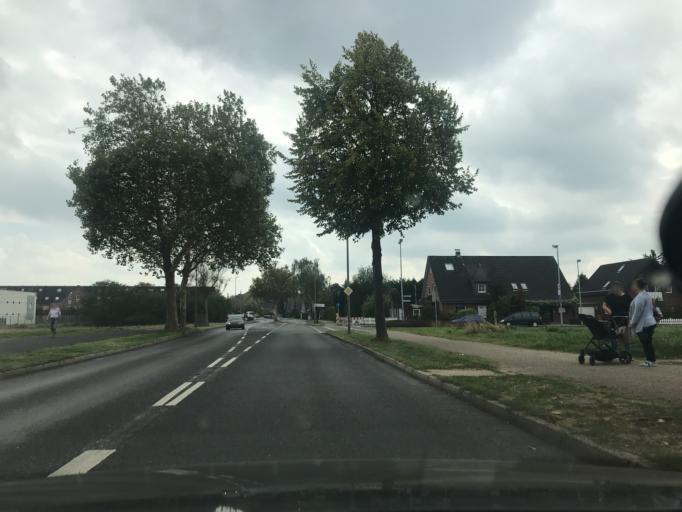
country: DE
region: North Rhine-Westphalia
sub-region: Regierungsbezirk Dusseldorf
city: Krefeld
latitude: 51.3694
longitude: 6.6364
